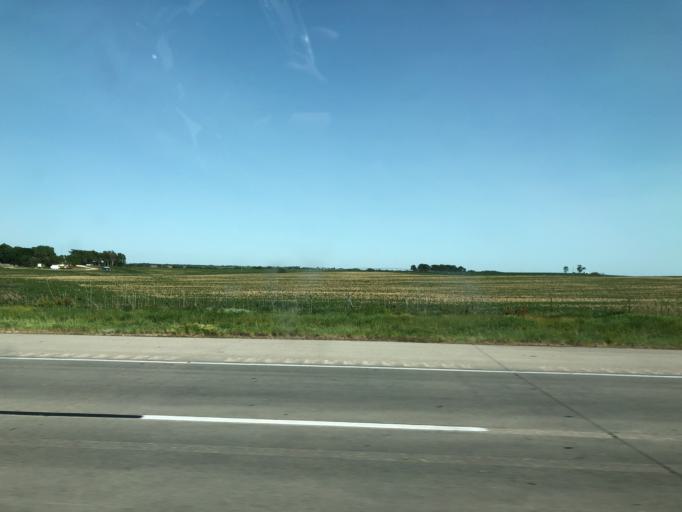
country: US
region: Nebraska
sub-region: Lancaster County
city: Waverly
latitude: 40.9359
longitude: -96.4347
